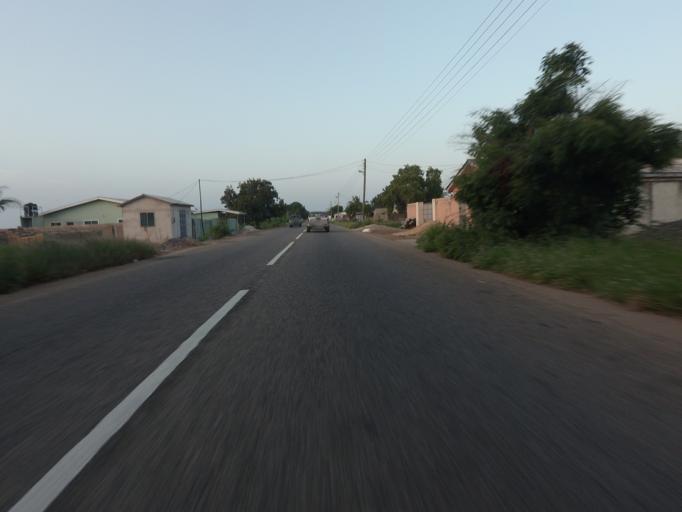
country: GH
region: Volta
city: Anloga
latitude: 5.8199
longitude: 0.9436
